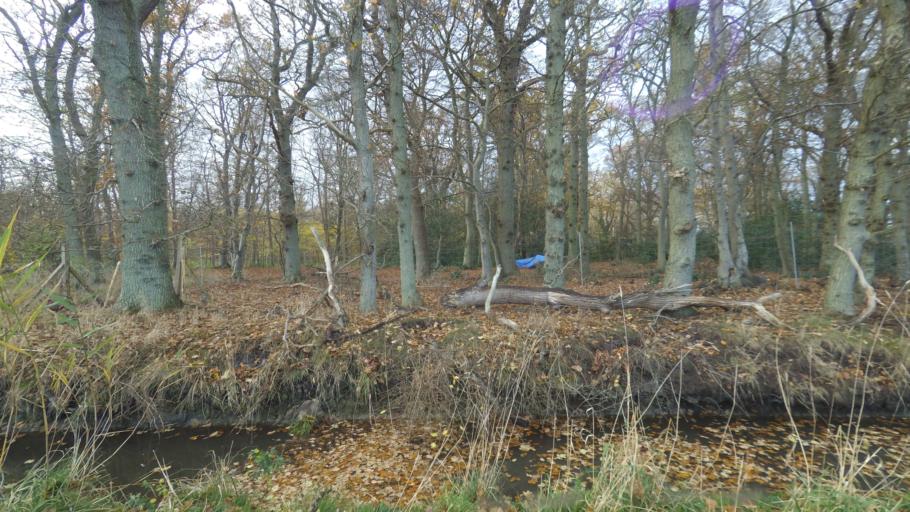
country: DK
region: Central Jutland
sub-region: Odder Kommune
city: Odder
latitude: 55.8425
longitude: 10.1938
